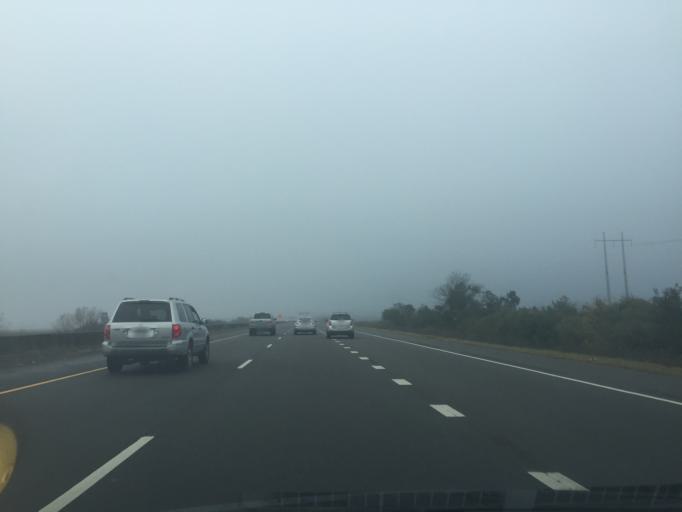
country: US
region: Georgia
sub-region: Chatham County
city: Georgetown
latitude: 31.9841
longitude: -81.1885
